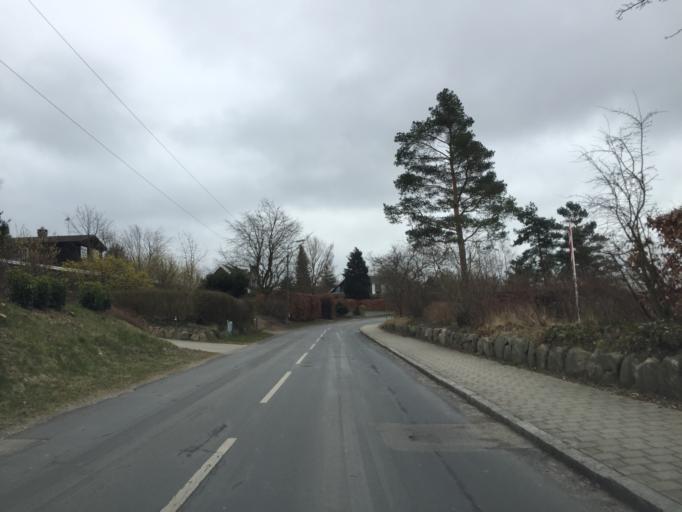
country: DK
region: Capital Region
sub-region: Allerod Kommune
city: Lillerod
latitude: 55.9060
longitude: 12.3301
